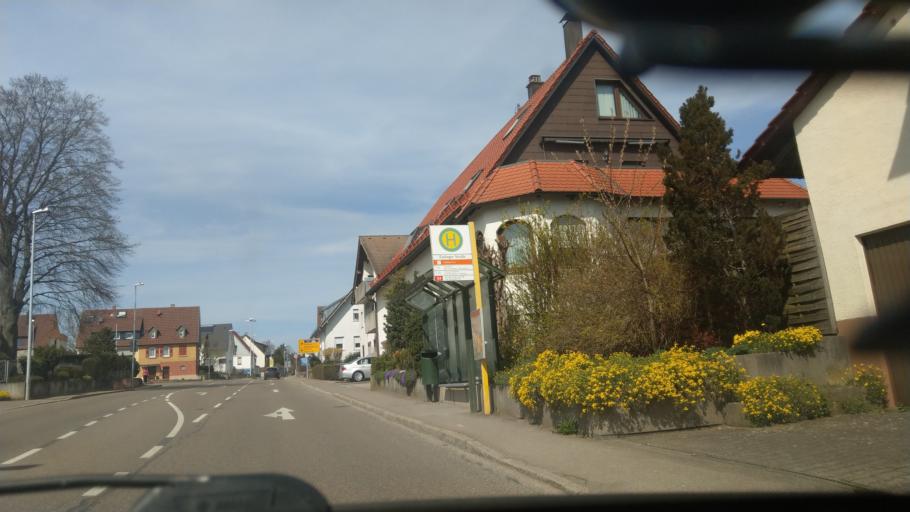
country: DE
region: Baden-Wuerttemberg
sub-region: Regierungsbezirk Stuttgart
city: Wolfschlugen
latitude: 48.6570
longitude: 9.2858
